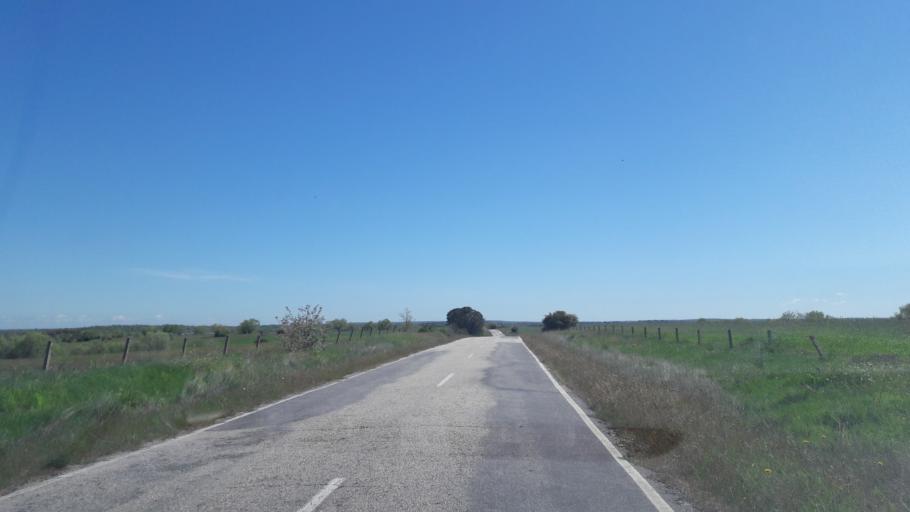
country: ES
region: Castille and Leon
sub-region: Provincia de Salamanca
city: Vitigudino
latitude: 41.0240
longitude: -6.4133
